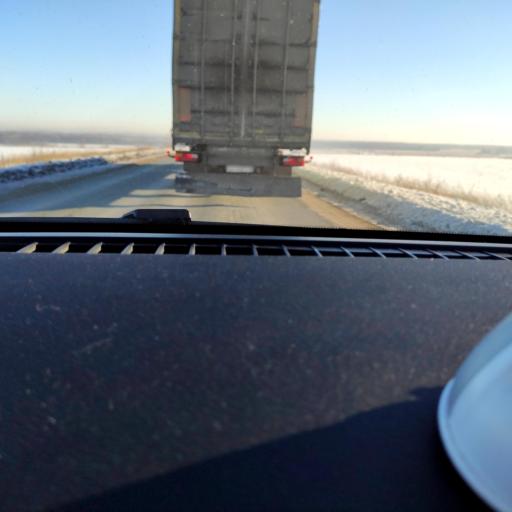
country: RU
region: Samara
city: Spiridonovka
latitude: 53.1445
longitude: 50.5799
